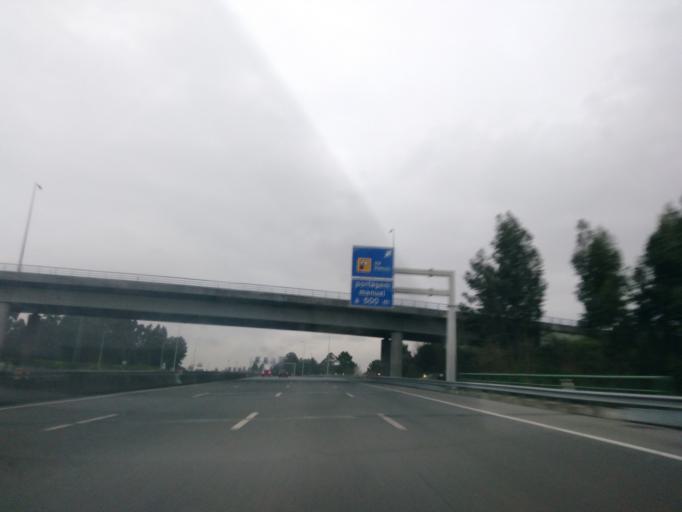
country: PT
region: Porto
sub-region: Valongo
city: Ermesinde
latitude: 41.2392
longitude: -8.5641
